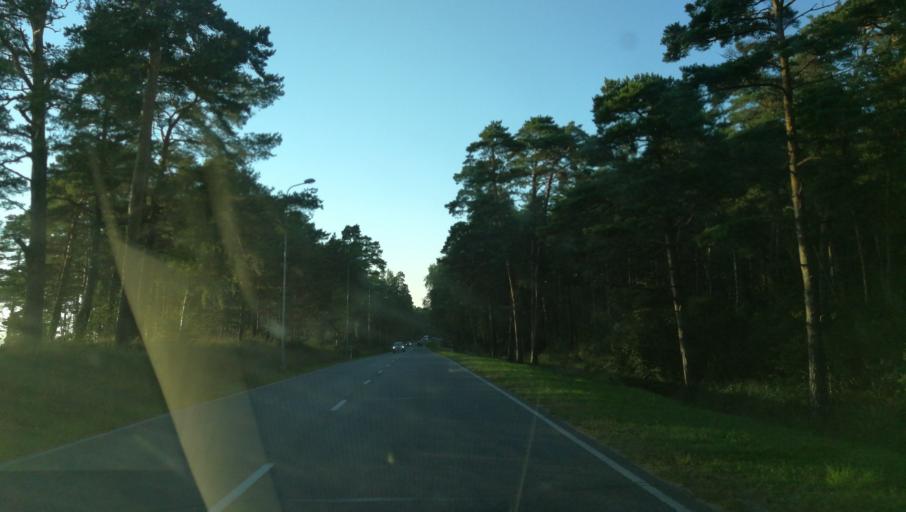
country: LV
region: Saulkrastu
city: Saulkrasti
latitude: 57.2891
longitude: 24.4120
